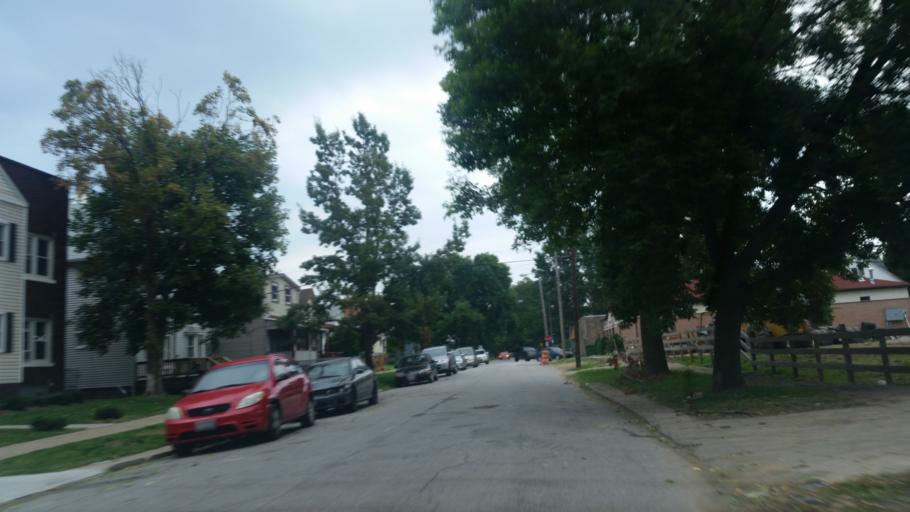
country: US
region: Ohio
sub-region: Cuyahoga County
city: Cleveland
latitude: 41.4725
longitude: -81.7091
